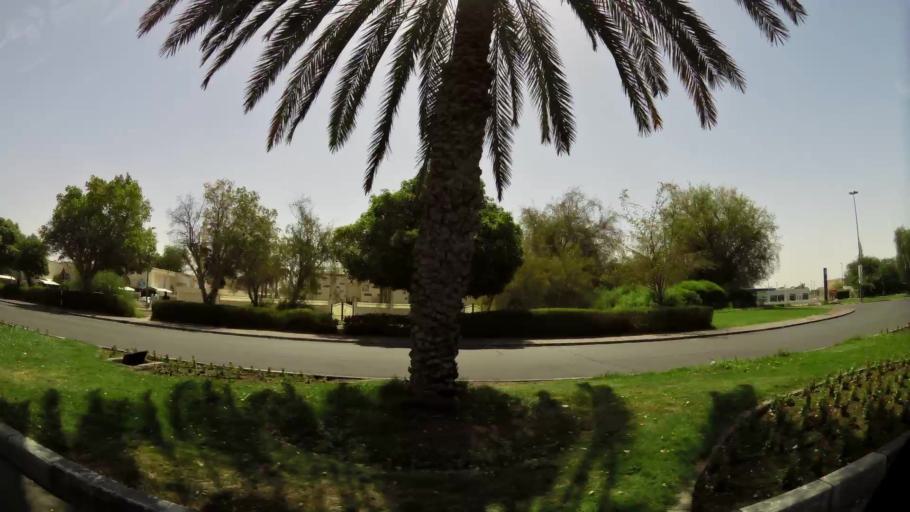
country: OM
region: Al Buraimi
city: Al Buraymi
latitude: 24.2877
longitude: 55.7675
